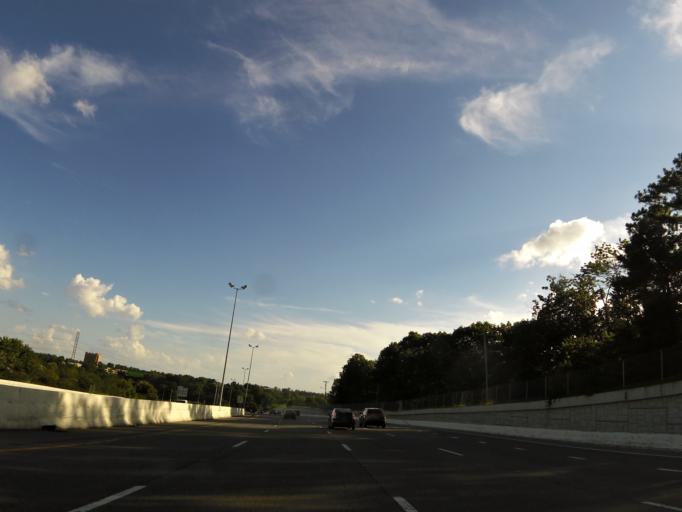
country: US
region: Tennessee
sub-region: Davidson County
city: Nashville
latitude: 36.1615
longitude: -86.6912
